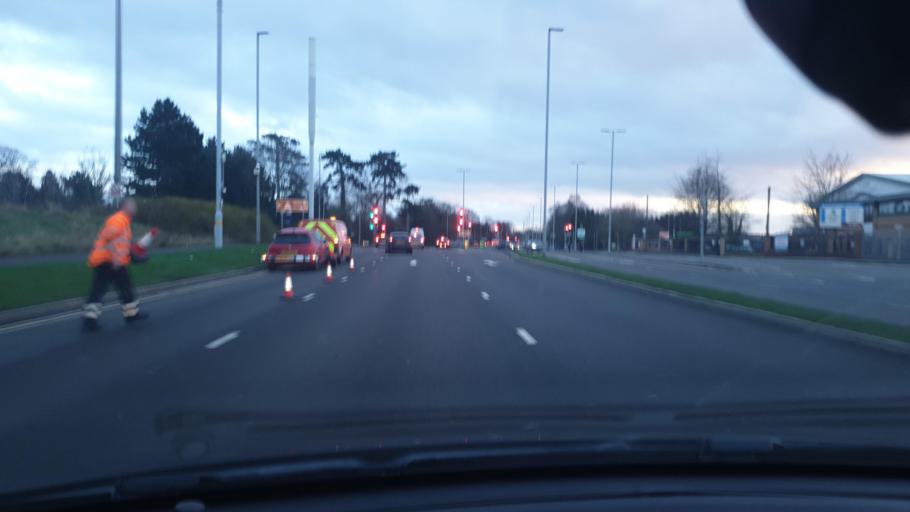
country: GB
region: England
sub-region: Staffordshire
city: Featherstone
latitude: 52.6365
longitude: -2.1252
